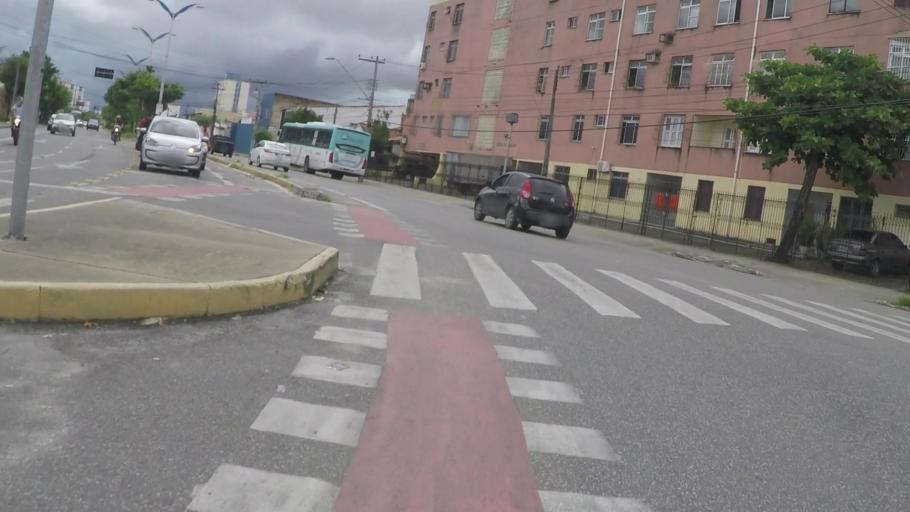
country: BR
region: Ceara
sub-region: Fortaleza
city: Fortaleza
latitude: -3.7328
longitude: -38.5422
